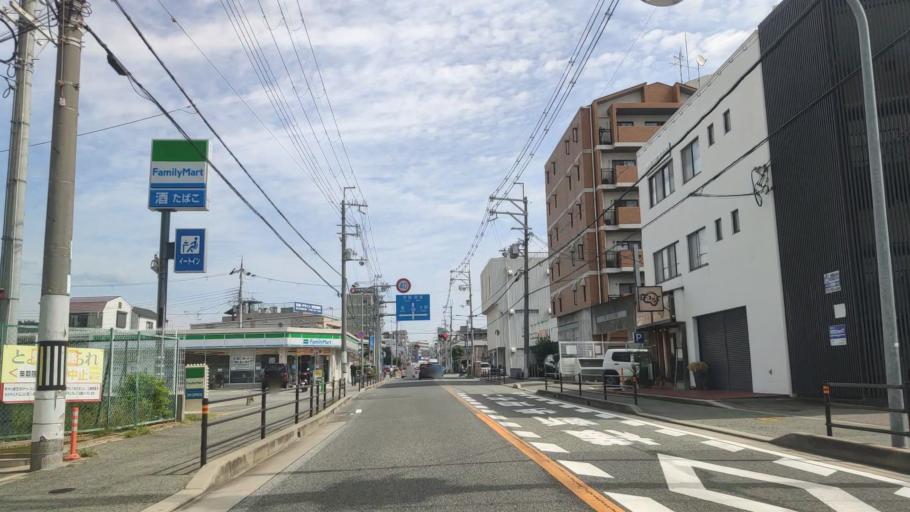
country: JP
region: Osaka
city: Ikeda
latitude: 34.8043
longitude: 135.4392
